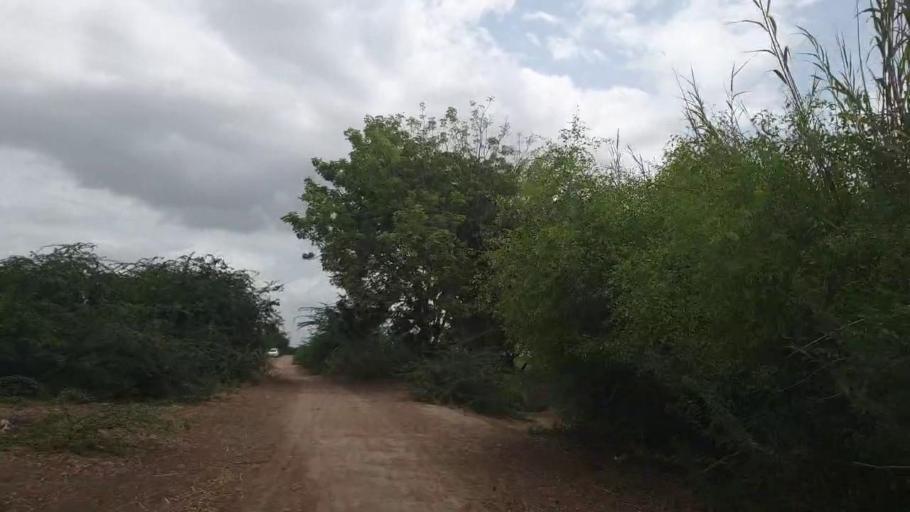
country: PK
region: Sindh
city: Badin
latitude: 24.6336
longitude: 68.9482
